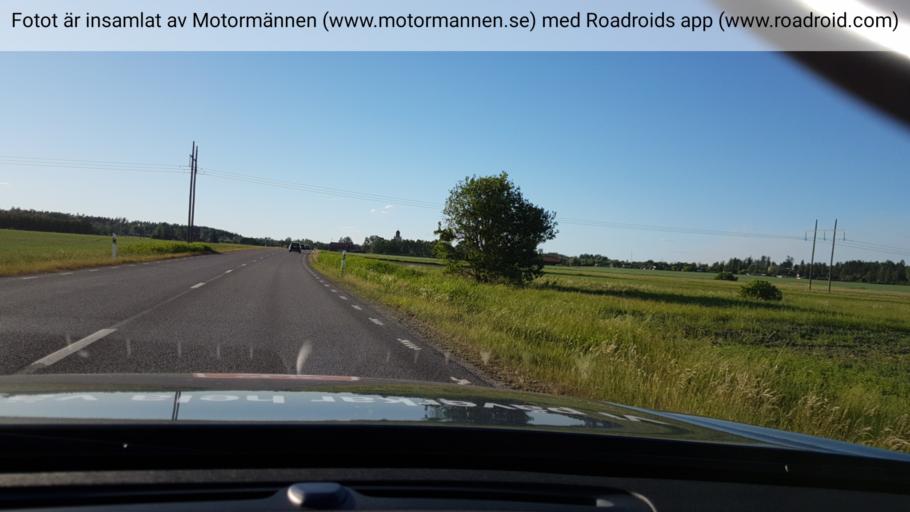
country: SE
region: Vaestmanland
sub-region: Hallstahammars Kommun
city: Kolback
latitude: 59.5503
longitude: 16.2333
